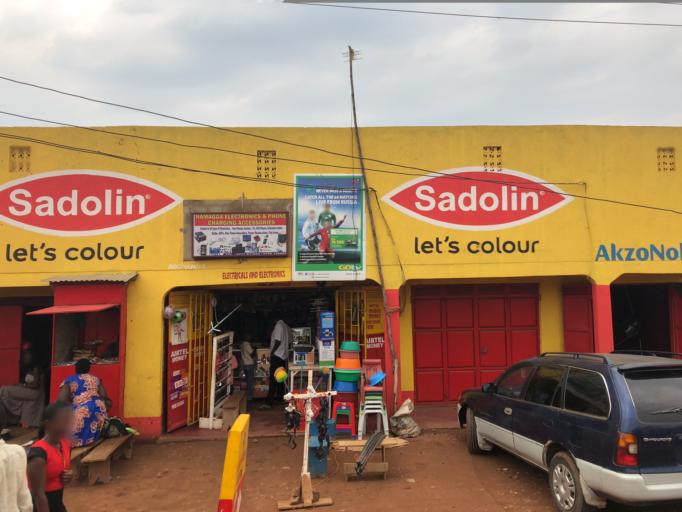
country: UG
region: Central Region
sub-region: Mukono District
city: Mukono
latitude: 0.3526
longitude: 32.7565
